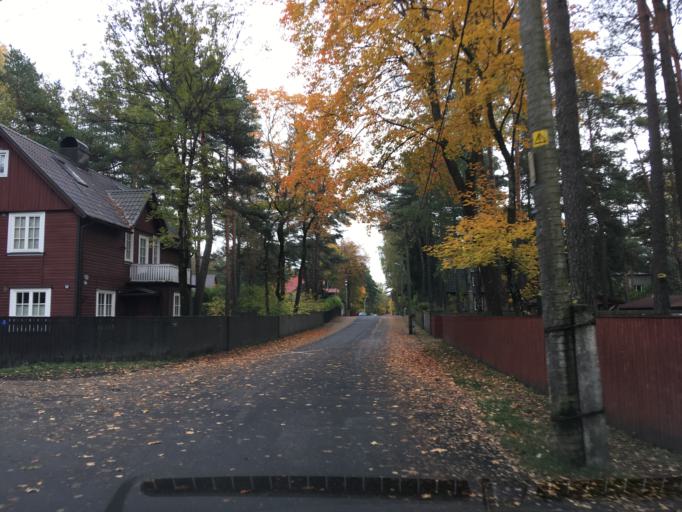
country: EE
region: Harju
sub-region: Tallinna linn
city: Tallinn
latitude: 59.3847
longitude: 24.6994
